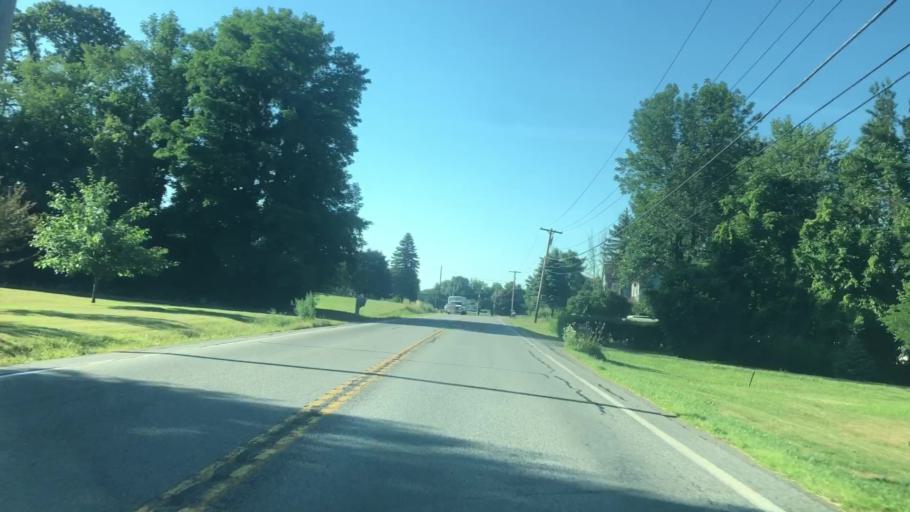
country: US
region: New York
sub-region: Wayne County
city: Ontario
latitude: 43.1884
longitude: -77.2914
